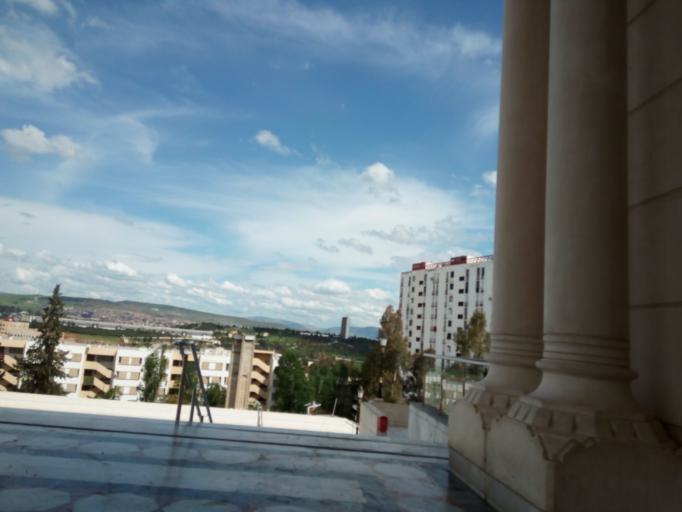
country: DZ
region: Constantine
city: Constantine
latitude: 36.3474
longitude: 6.6036
